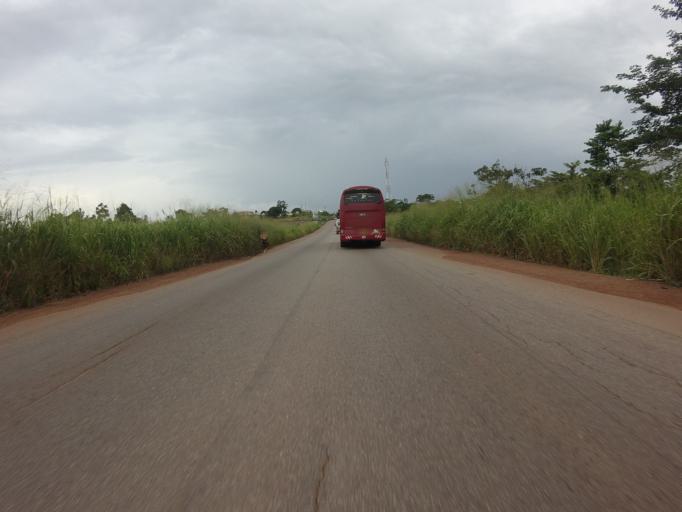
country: GH
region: Ashanti
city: Konongo
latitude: 6.6175
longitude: -1.1857
